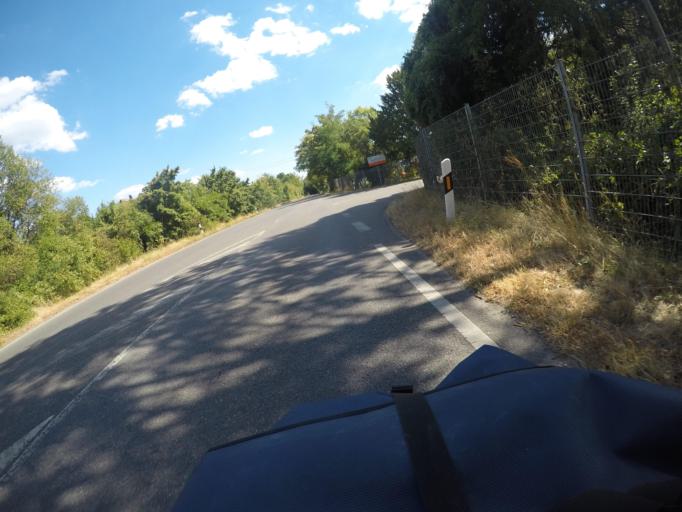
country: DE
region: Rheinland-Pfalz
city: Gartenstadt
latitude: 49.4796
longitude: 8.4064
